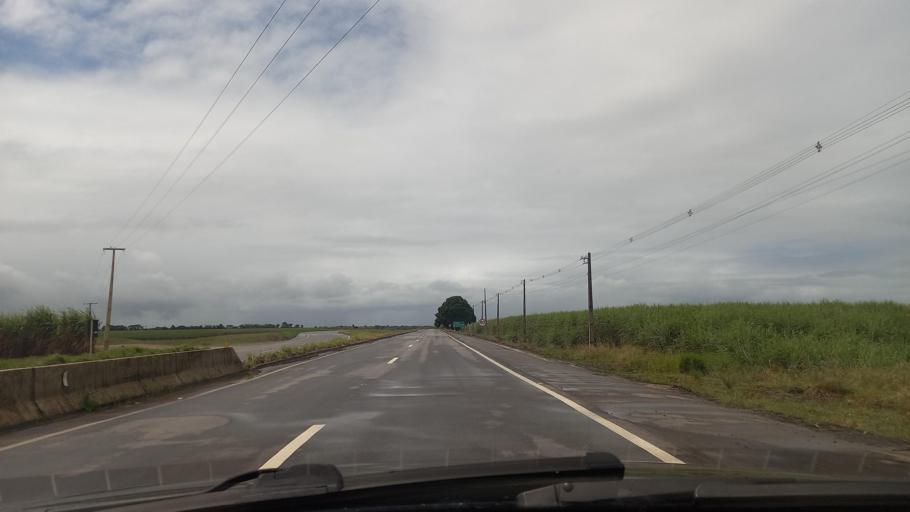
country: BR
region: Alagoas
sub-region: Campo Alegre
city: Campo Alegre
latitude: -9.8229
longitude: -36.2398
